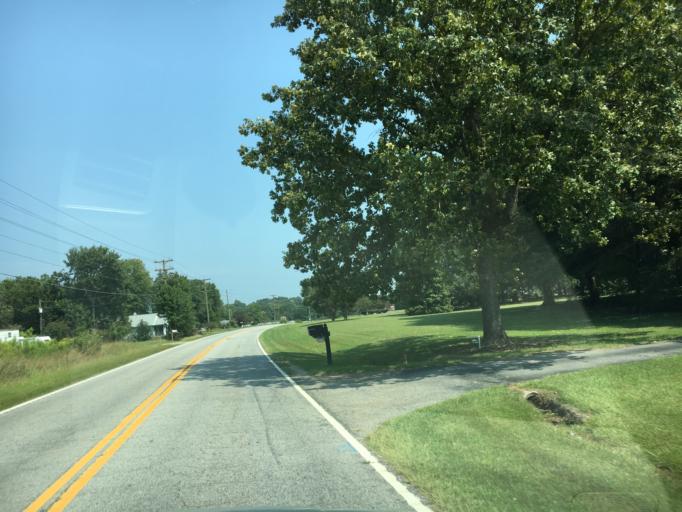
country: US
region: South Carolina
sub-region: Spartanburg County
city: Boiling Springs
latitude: 35.0677
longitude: -81.9323
